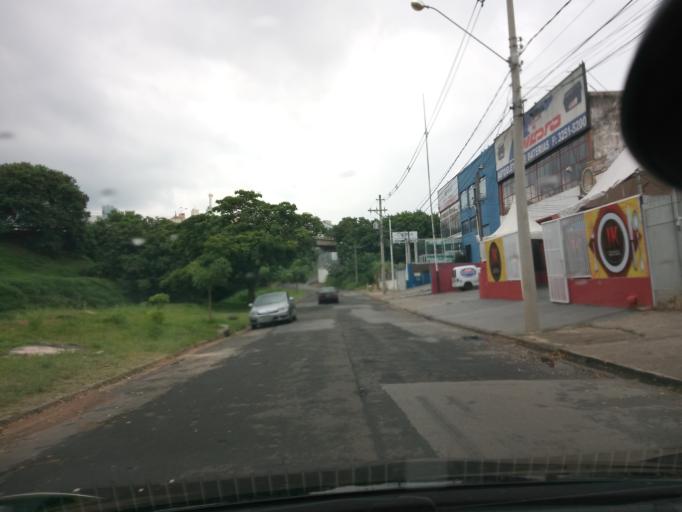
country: BR
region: Sao Paulo
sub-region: Campinas
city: Campinas
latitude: -22.8839
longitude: -47.0433
